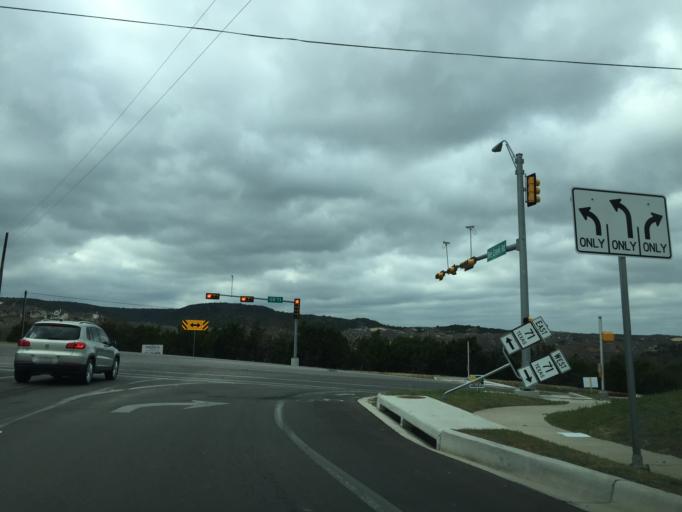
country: US
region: Texas
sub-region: Travis County
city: The Hills
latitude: 30.3319
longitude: -98.0243
